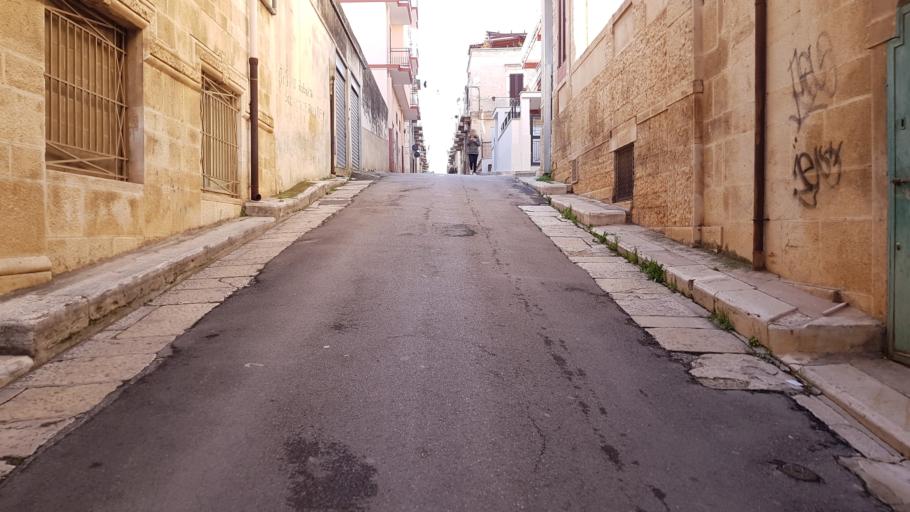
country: IT
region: Apulia
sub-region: Provincia di Bari
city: Ruvo di Puglia
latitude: 41.1187
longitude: 16.4883
